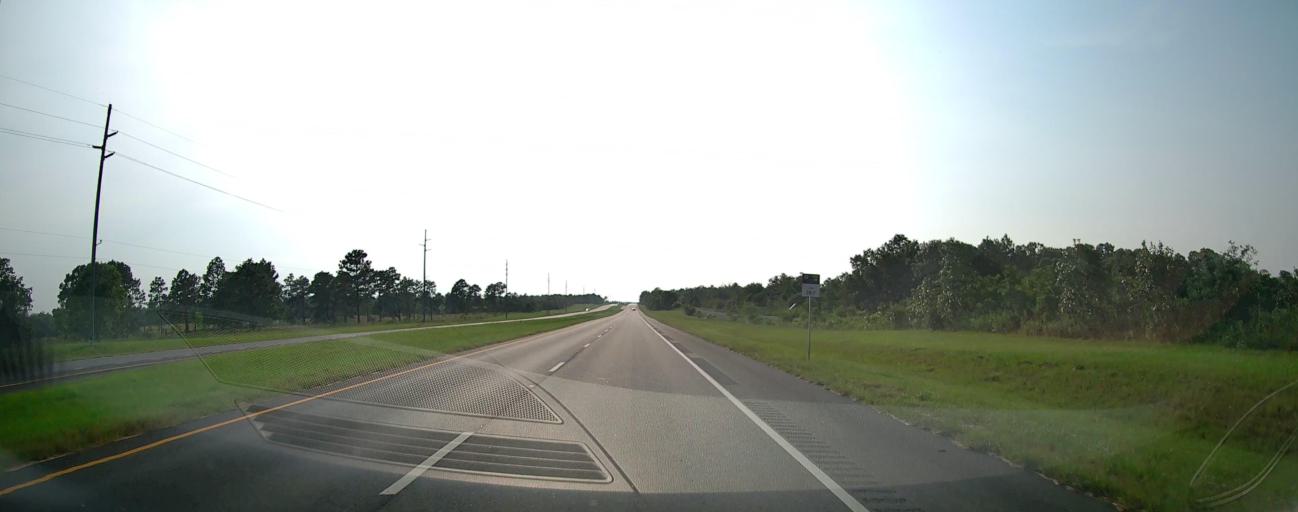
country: US
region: Georgia
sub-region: Taylor County
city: Butler
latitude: 32.5844
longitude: -84.3371
